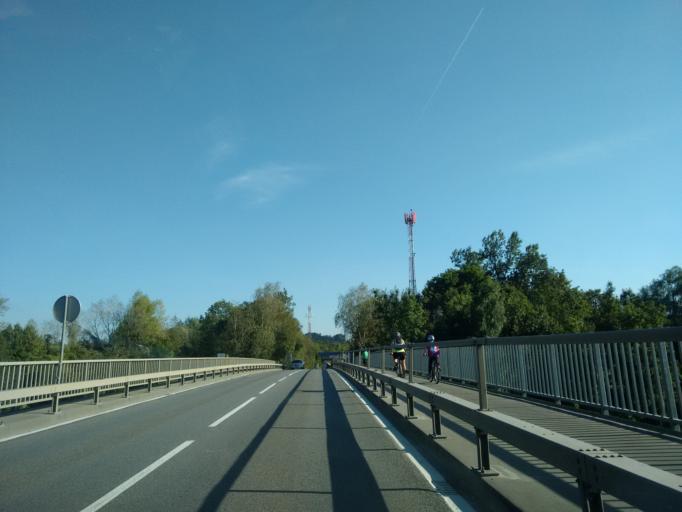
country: AT
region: Upper Austria
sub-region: Wels-Land
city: Marchtrenk
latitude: 48.1769
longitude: 14.1196
